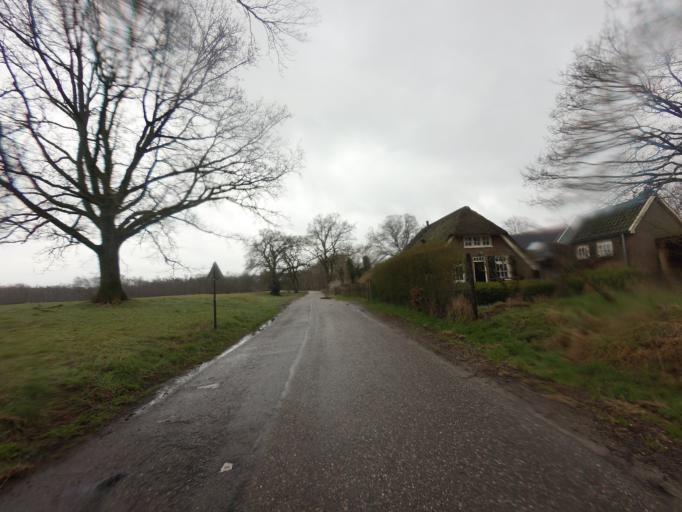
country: NL
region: Gelderland
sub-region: Gemeente Epe
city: Vaassen
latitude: 52.3125
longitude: 5.8955
